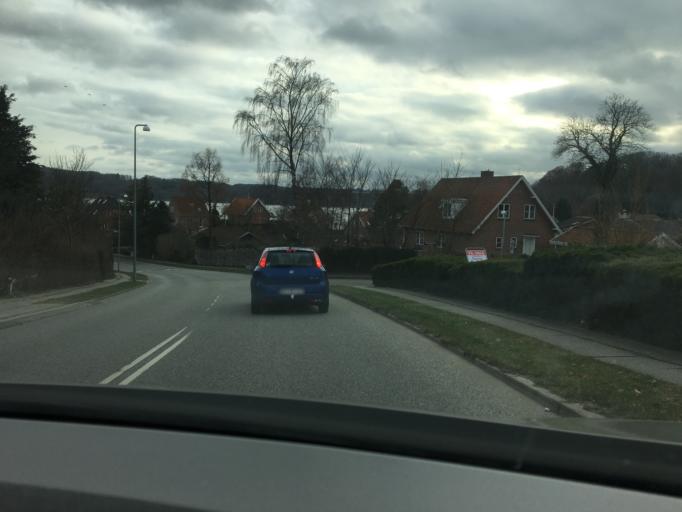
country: DK
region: South Denmark
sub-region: Vejle Kommune
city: Vejle
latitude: 55.7084
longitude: 9.5894
